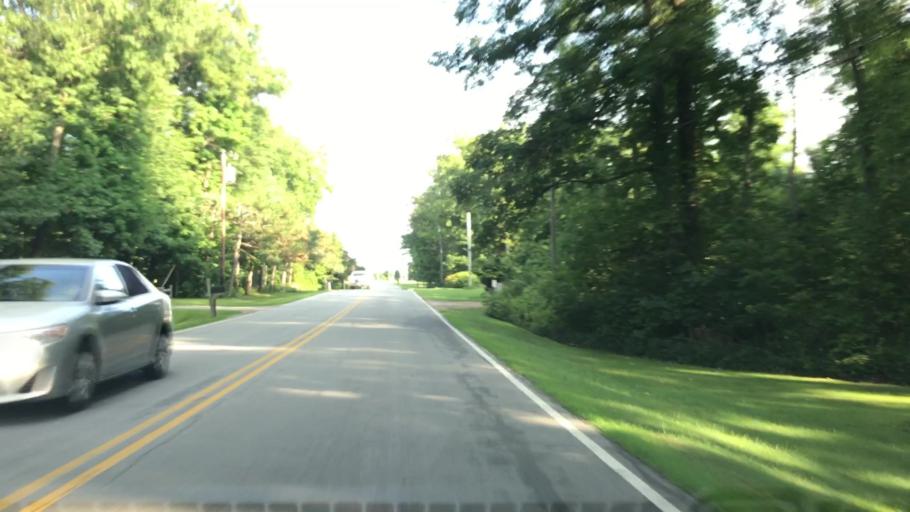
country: US
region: Ohio
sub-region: Union County
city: Marysville
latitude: 40.1938
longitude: -83.3369
